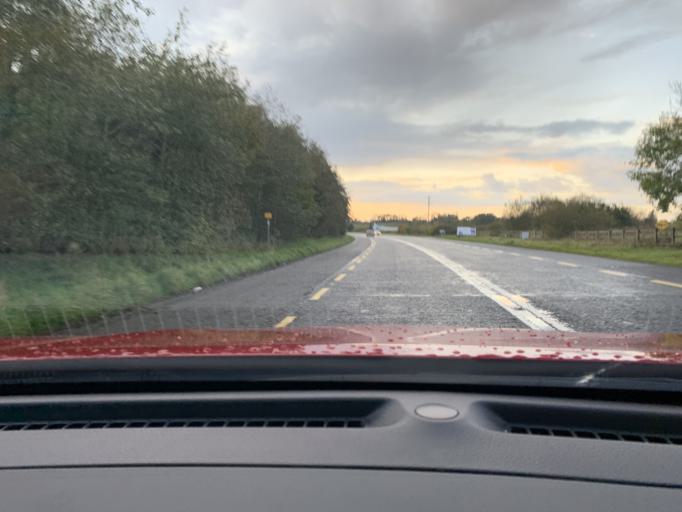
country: IE
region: Connaught
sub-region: County Leitrim
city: Carrick-on-Shannon
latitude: 53.9488
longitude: -8.1286
